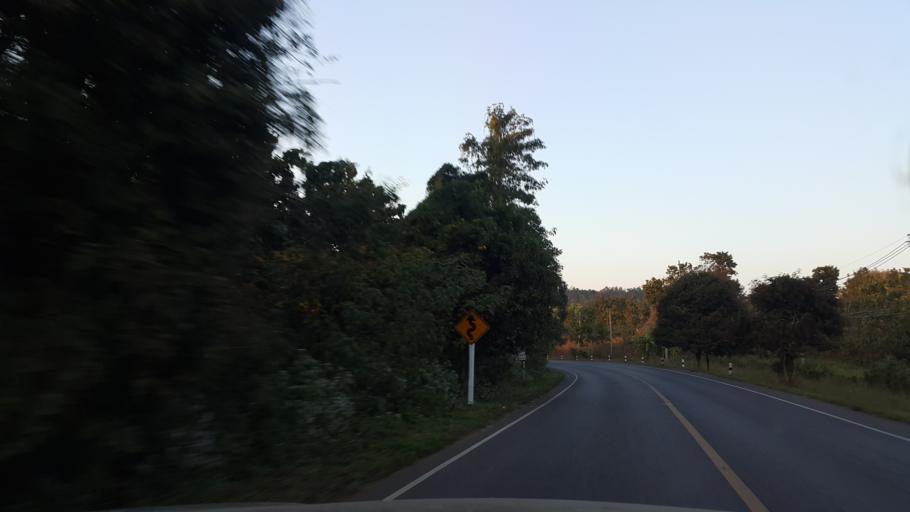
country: TH
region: Phrae
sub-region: Amphoe Wang Chin
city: Wang Chin
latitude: 17.8442
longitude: 99.6414
